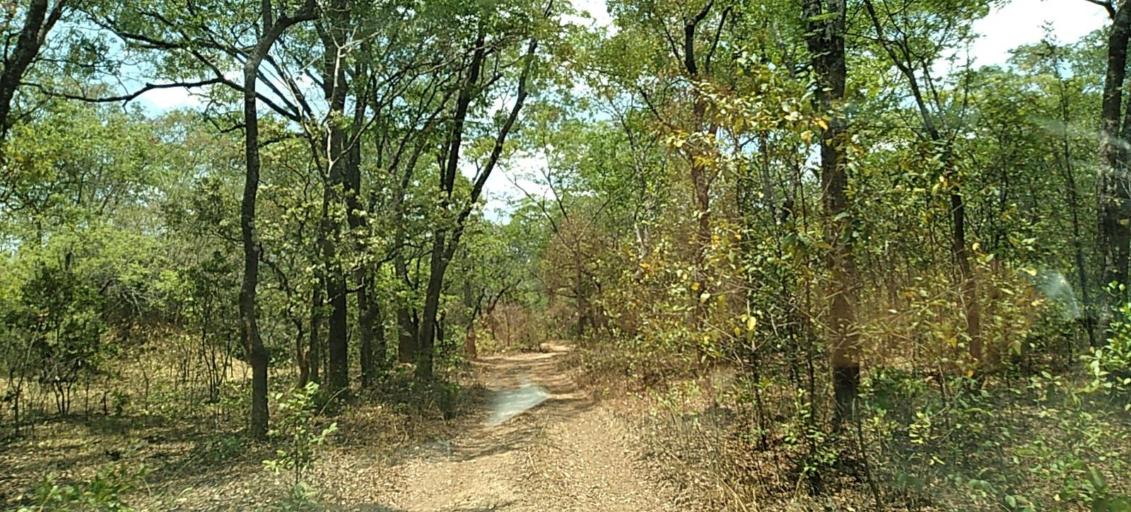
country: ZM
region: Copperbelt
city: Chililabombwe
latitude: -12.4662
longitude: 27.6993
